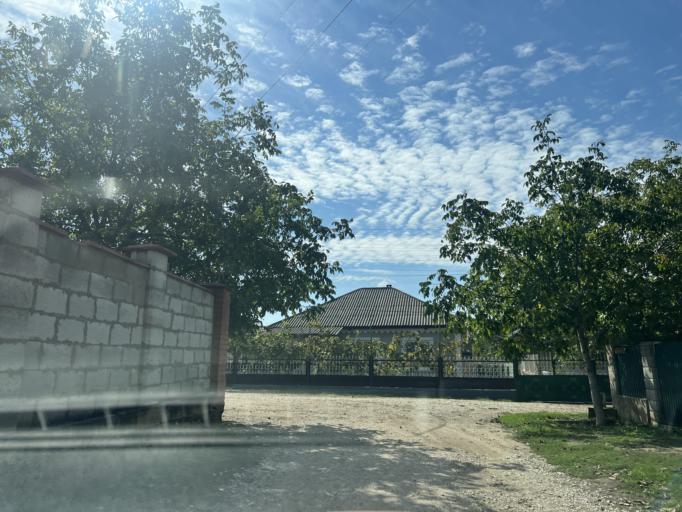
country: MD
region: Ungheni
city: Ungheni
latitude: 47.2025
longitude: 27.8126
